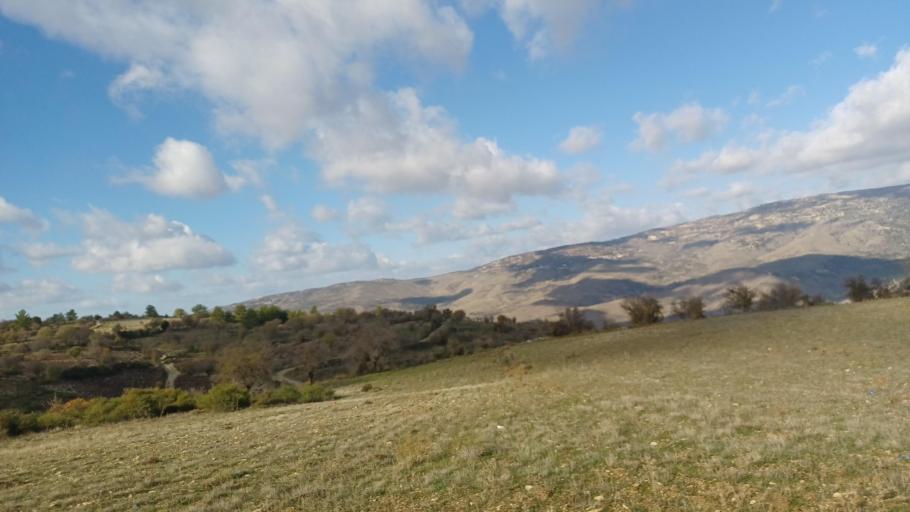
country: CY
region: Limassol
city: Pachna
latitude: 34.8560
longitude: 32.6909
